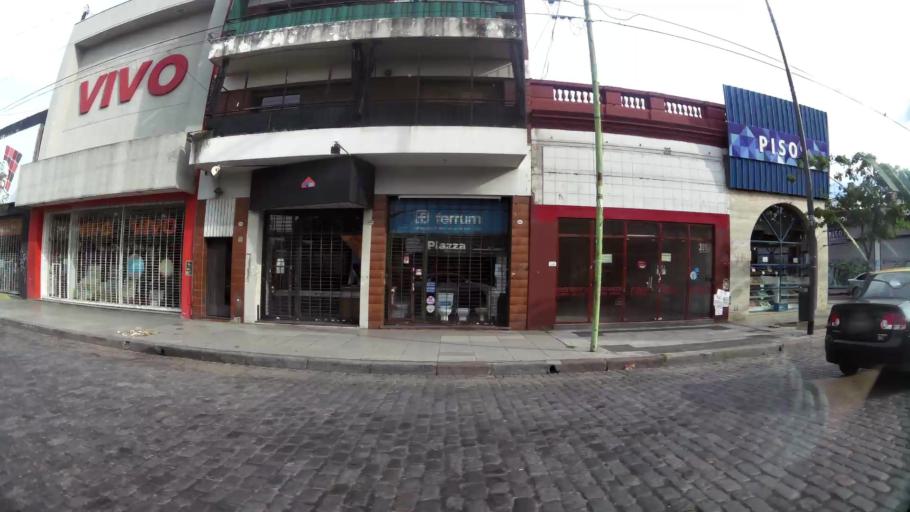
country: AR
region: Buenos Aires F.D.
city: Villa Santa Rita
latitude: -34.6384
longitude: -58.4812
